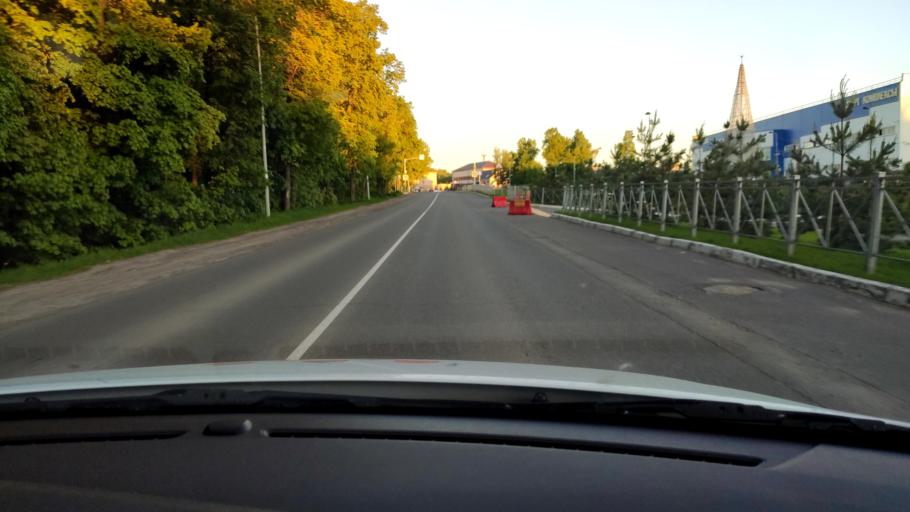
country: RU
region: Tatarstan
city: Vysokaya Gora
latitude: 55.9241
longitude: 49.3046
